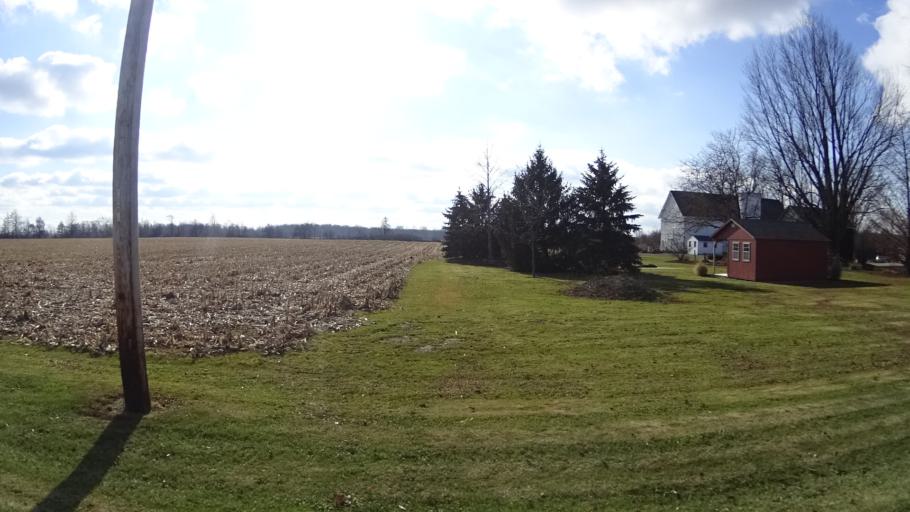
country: US
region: Ohio
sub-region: Lorain County
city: Camden
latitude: 41.2583
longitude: -82.2778
